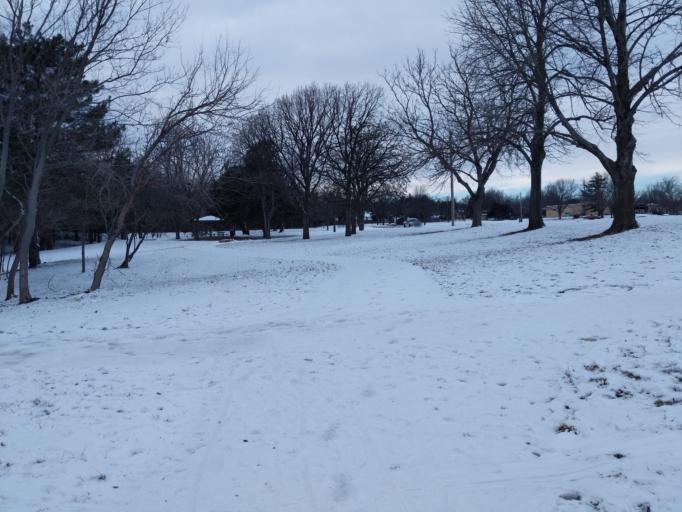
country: US
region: Kansas
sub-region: Riley County
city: Manhattan
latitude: 39.1974
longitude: -96.6204
